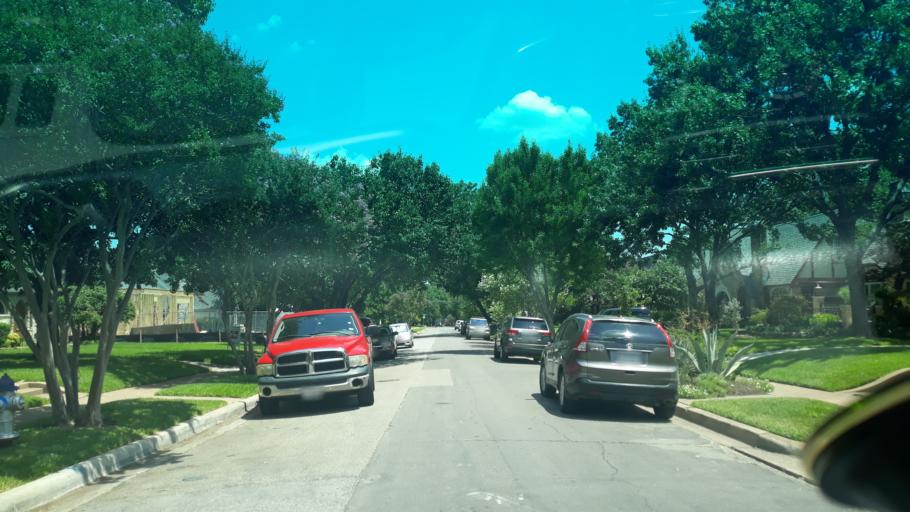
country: US
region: Texas
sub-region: Dallas County
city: Highland Park
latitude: 32.8225
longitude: -96.7402
